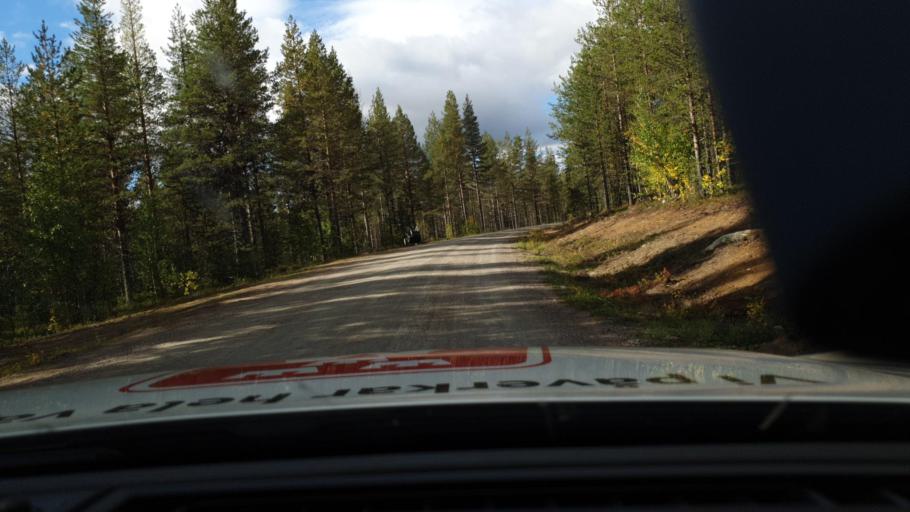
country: FI
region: Lapland
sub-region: Tunturi-Lappi
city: Kolari
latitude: 67.4362
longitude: 23.6875
